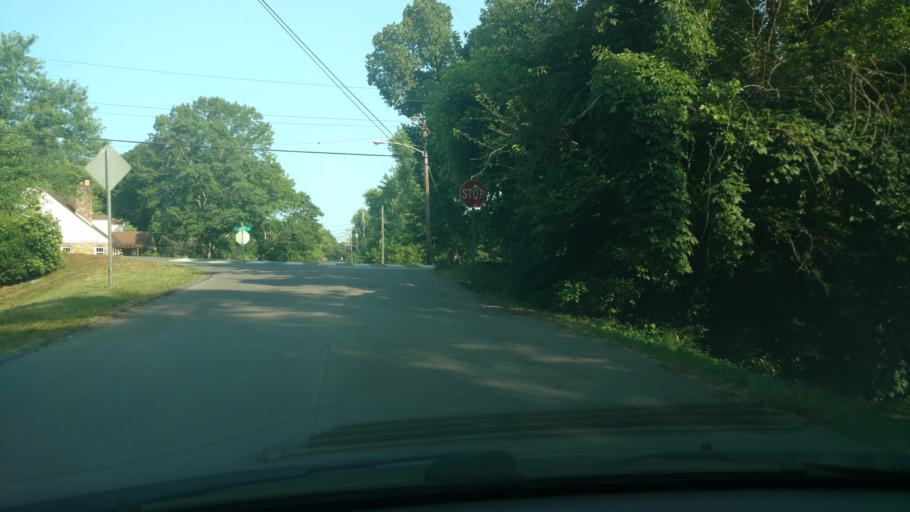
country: US
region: Tennessee
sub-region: Davidson County
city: Nashville
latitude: 36.2146
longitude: -86.7201
